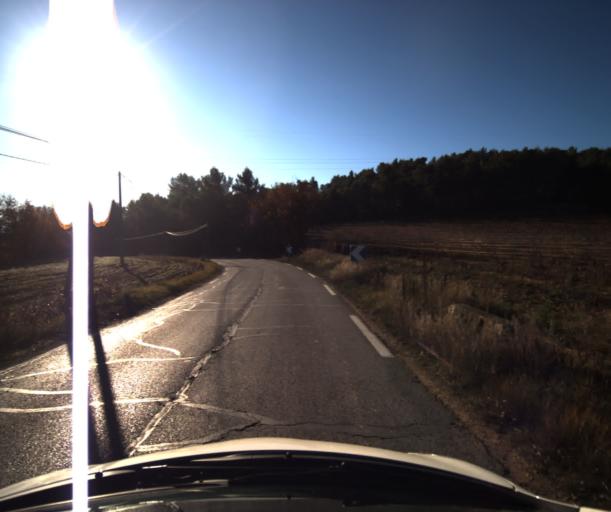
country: FR
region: Provence-Alpes-Cote d'Azur
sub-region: Departement du Vaucluse
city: Pertuis
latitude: 43.7193
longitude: 5.5041
